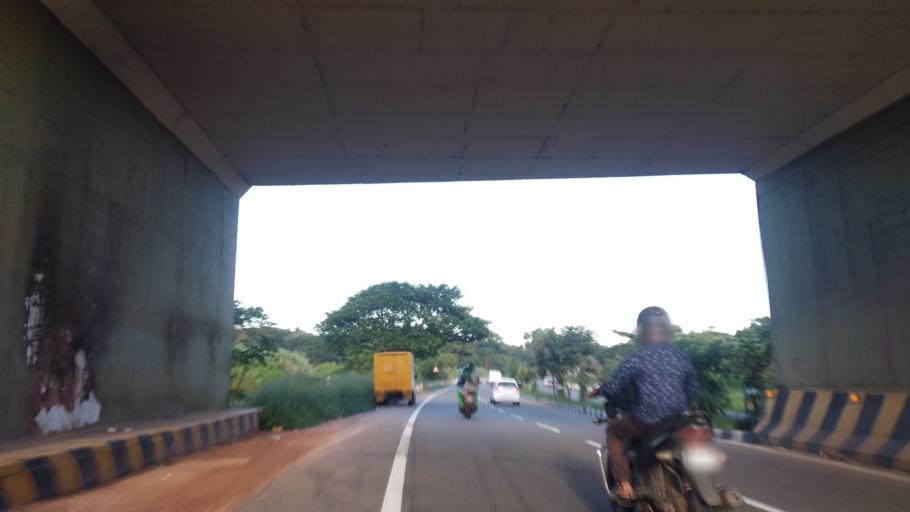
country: IN
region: Kerala
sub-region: Ernakulam
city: Elur
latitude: 10.0693
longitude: 76.3023
